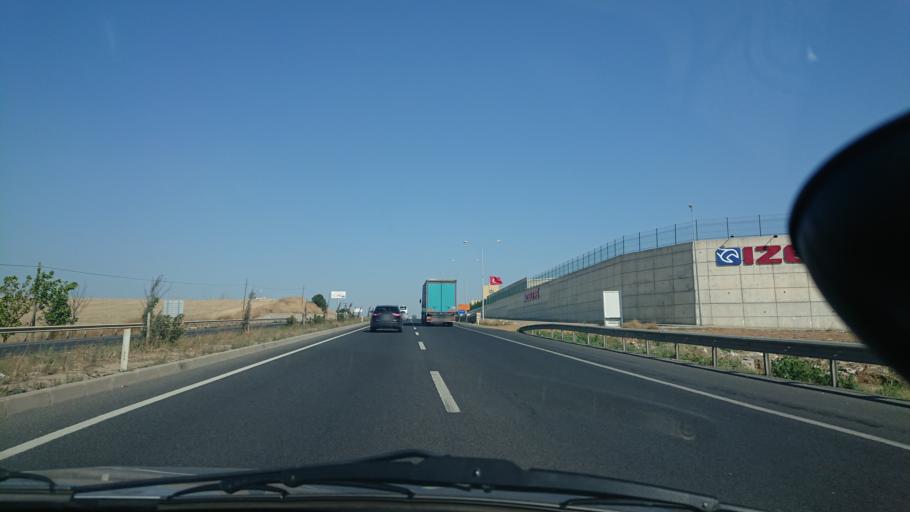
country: TR
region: Manisa
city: Turgutlu
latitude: 38.4884
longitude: 27.6360
